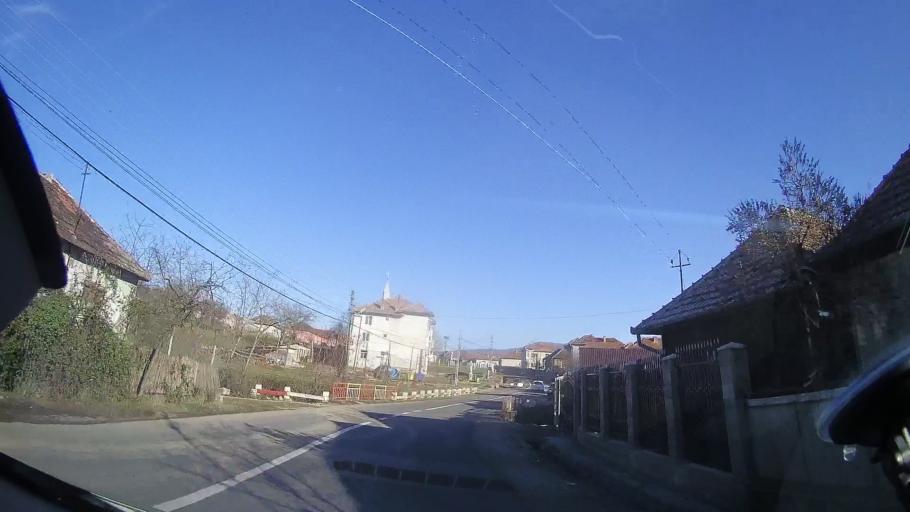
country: RO
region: Bihor
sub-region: Comuna Bratca
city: Beznea
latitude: 46.9577
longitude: 22.6160
